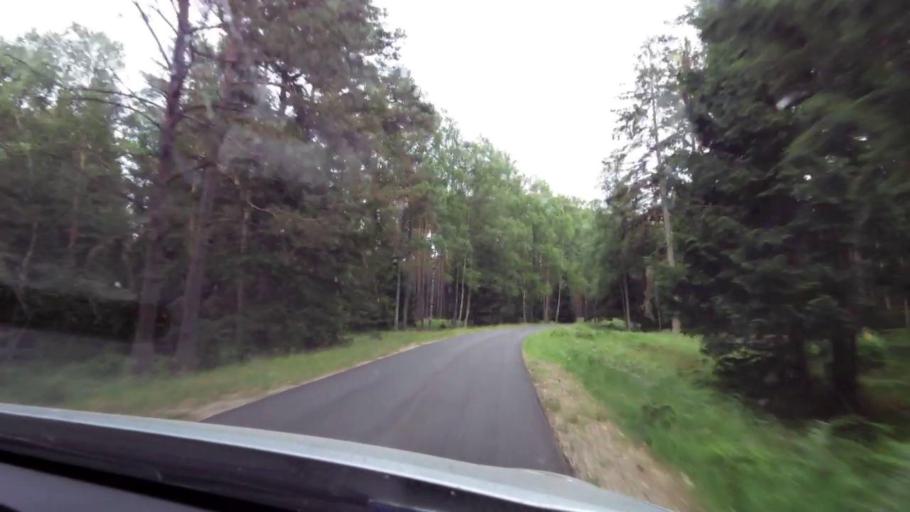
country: PL
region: Pomeranian Voivodeship
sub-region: Powiat bytowski
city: Trzebielino
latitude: 54.1976
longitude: 17.0442
